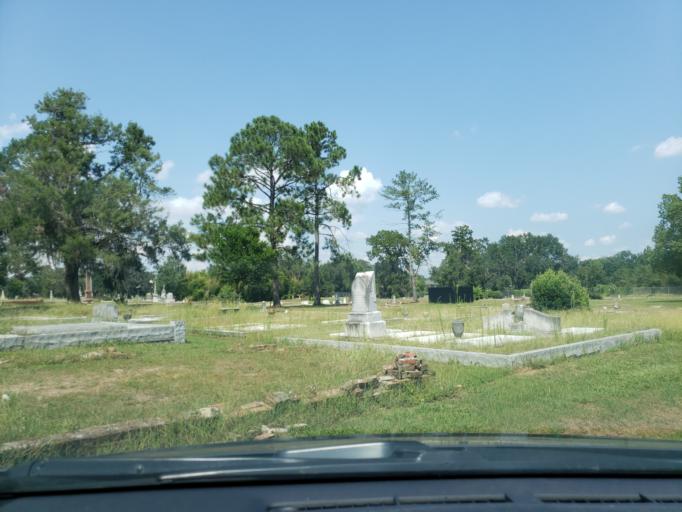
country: US
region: Georgia
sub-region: Dougherty County
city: Albany
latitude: 31.5688
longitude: -84.1526
